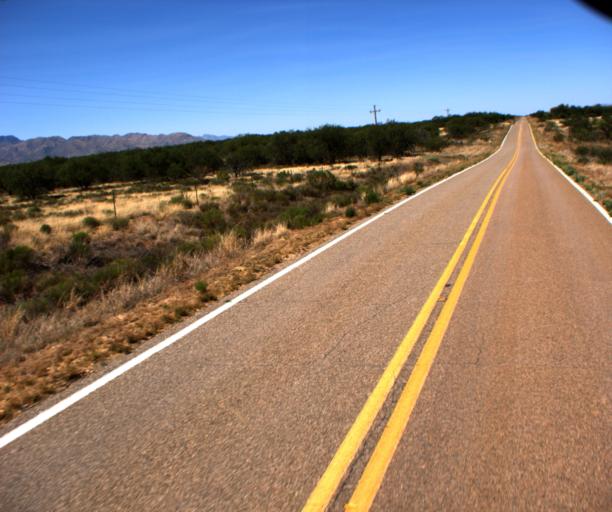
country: US
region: Arizona
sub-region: Pima County
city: Arivaca Junction
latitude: 31.6258
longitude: -111.5106
